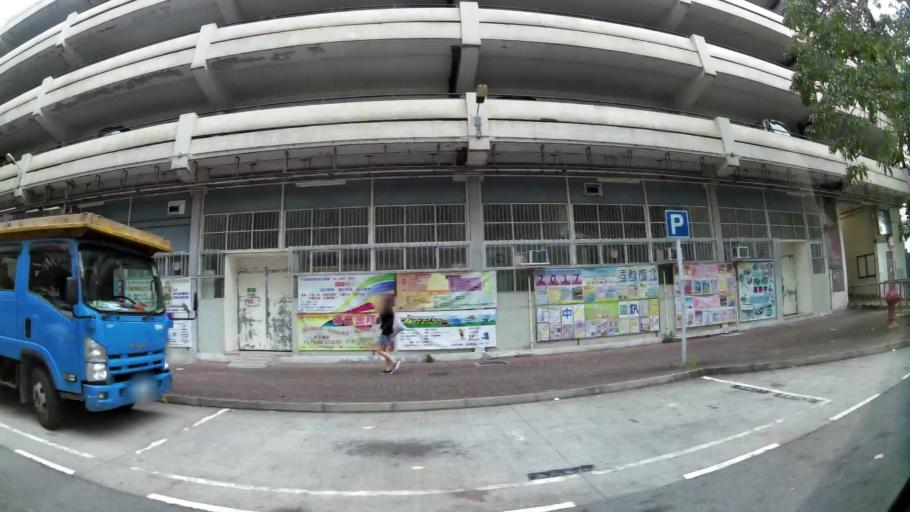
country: HK
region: Tai Po
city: Tai Po
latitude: 22.4553
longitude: 114.1701
